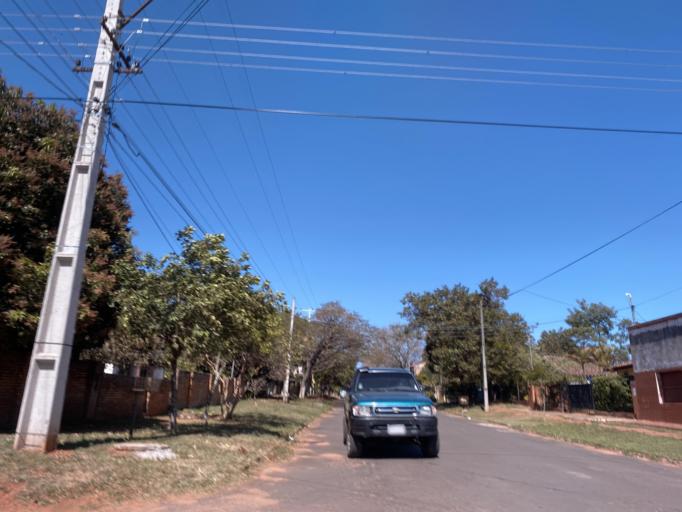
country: PY
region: Misiones
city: San Juan Bautista
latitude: -26.6653
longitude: -57.1476
